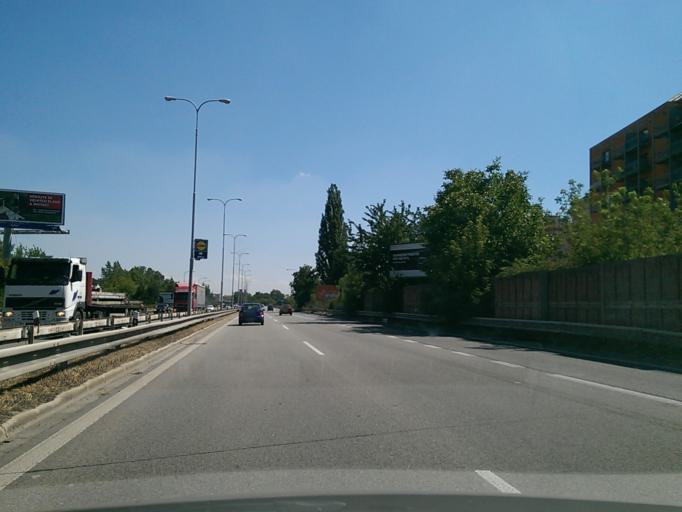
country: CZ
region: South Moravian
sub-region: Mesto Brno
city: Mokra Hora
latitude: 49.2344
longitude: 16.5918
